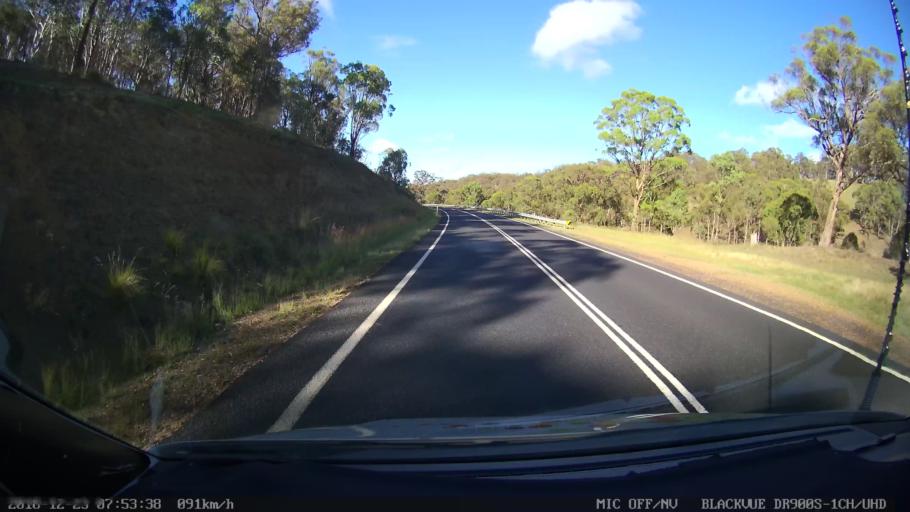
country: AU
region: New South Wales
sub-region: Armidale Dumaresq
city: Armidale
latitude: -30.5380
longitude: 151.8065
